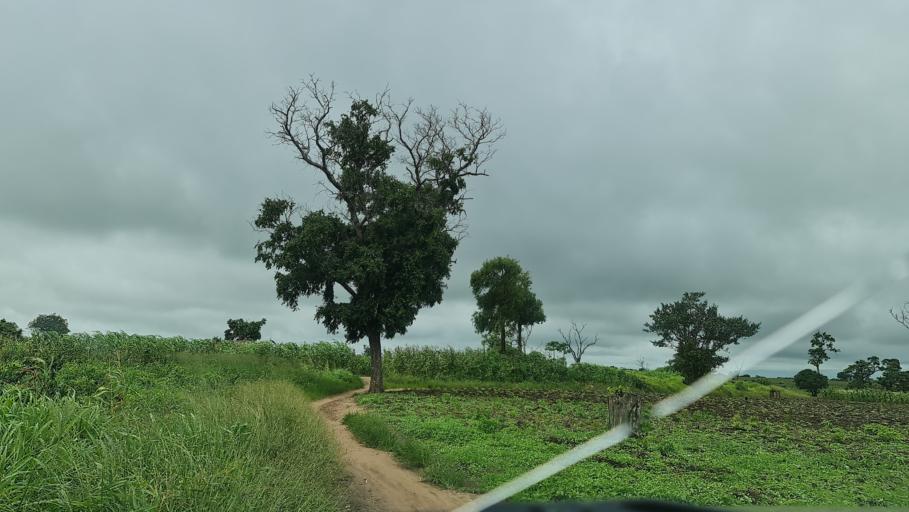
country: MW
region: Southern Region
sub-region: Nsanje District
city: Nsanje
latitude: -17.3390
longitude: 35.7199
